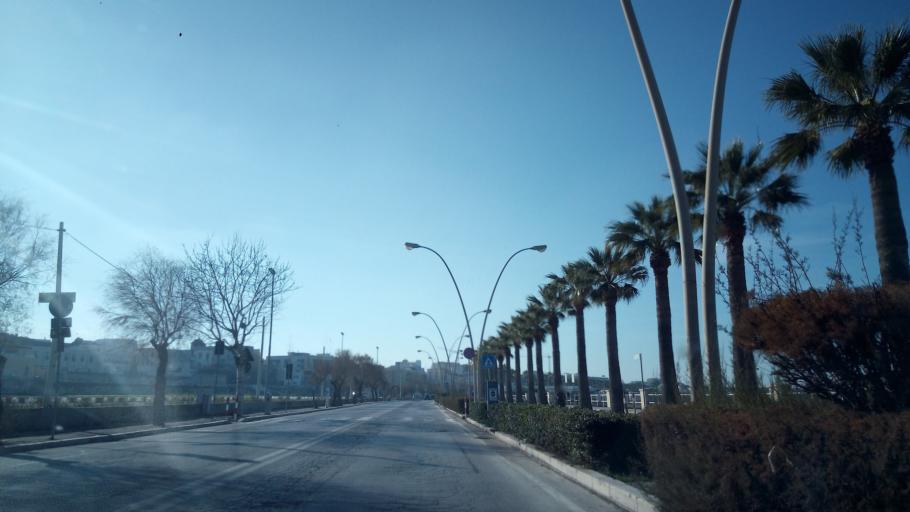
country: IT
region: Apulia
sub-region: Provincia di Barletta - Andria - Trani
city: Barletta
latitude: 41.3238
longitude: 16.2835
